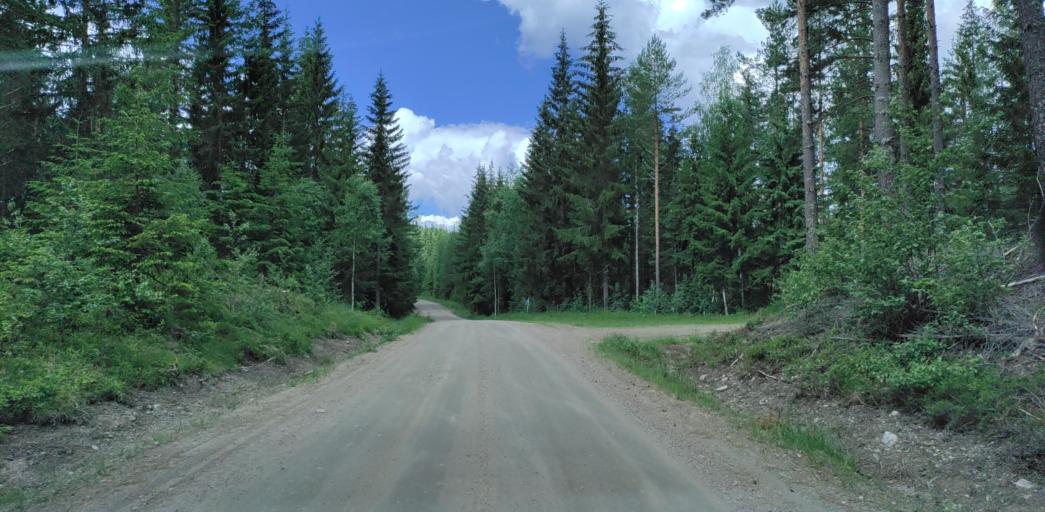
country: SE
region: Vaermland
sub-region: Hagfors Kommun
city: Ekshaerad
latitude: 60.1006
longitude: 13.3903
